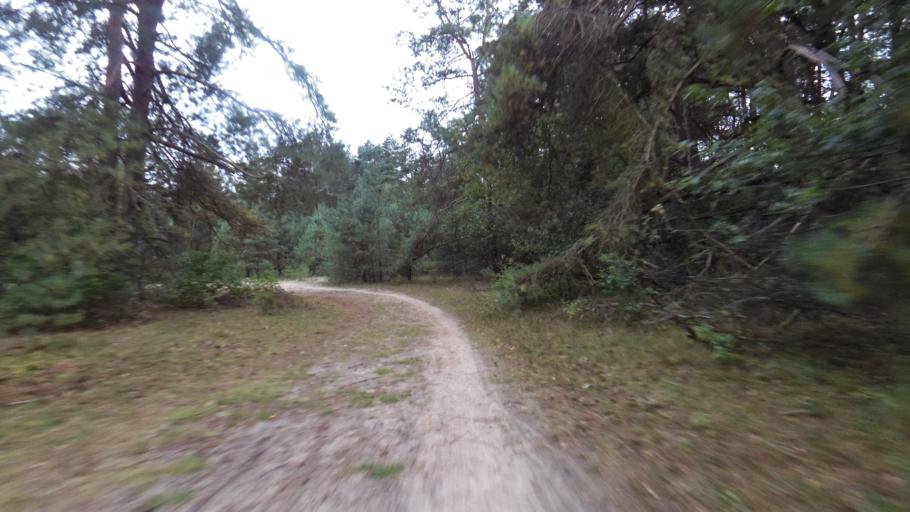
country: NL
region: Gelderland
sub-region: Gemeente Apeldoorn
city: Uddel
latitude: 52.1900
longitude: 5.8040
